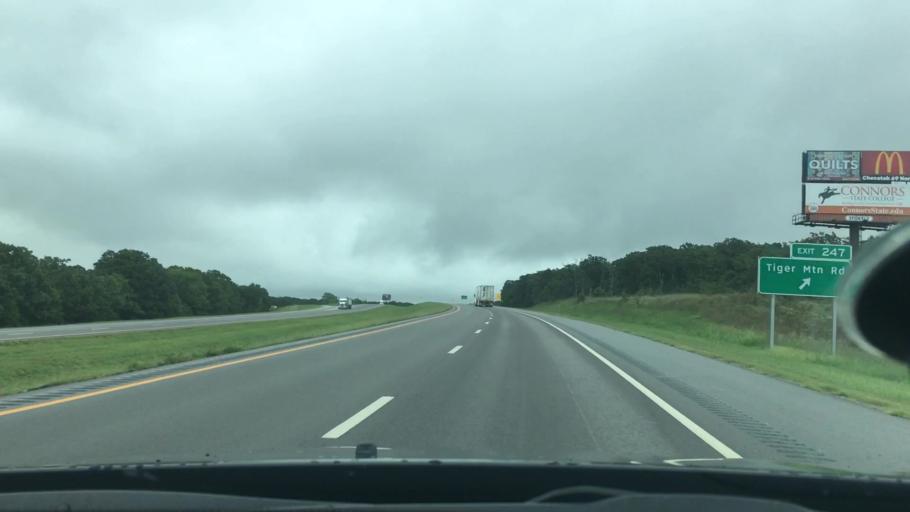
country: US
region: Oklahoma
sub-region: Okmulgee County
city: Henryetta
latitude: 35.4329
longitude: -95.8479
